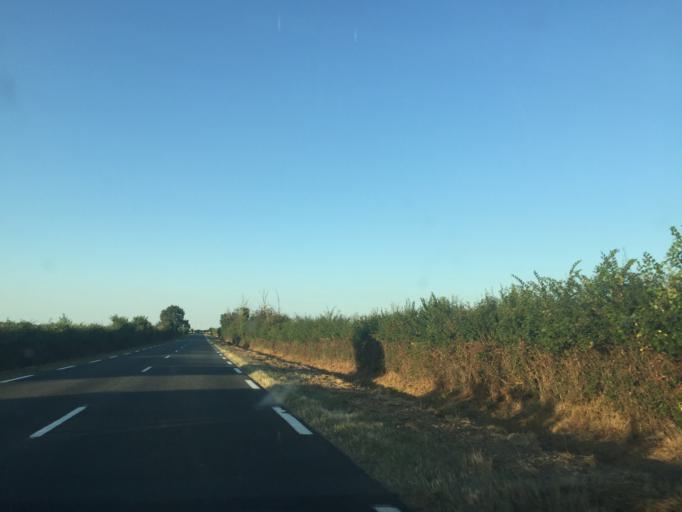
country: FR
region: Poitou-Charentes
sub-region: Departement de la Vienne
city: Saint-Sauvant
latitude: 46.3790
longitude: 0.0396
